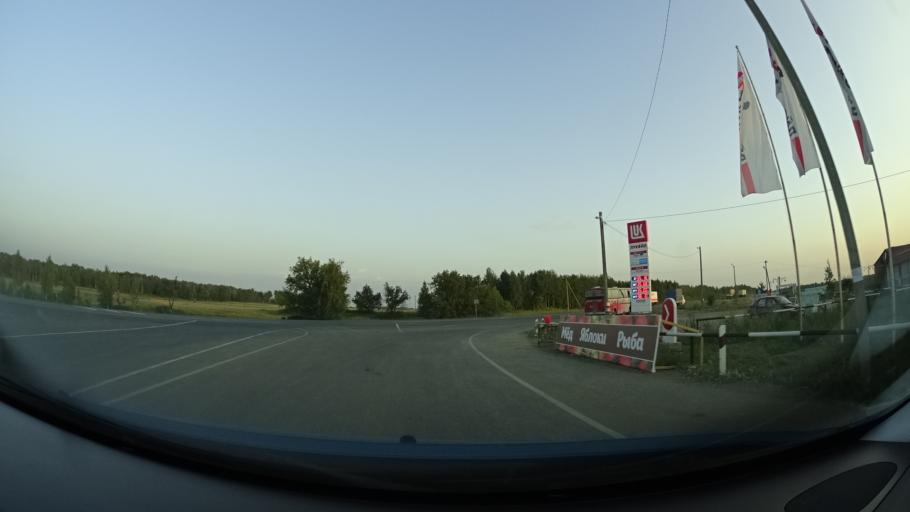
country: RU
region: Samara
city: Sernovodsk
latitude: 53.9322
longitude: 51.3316
